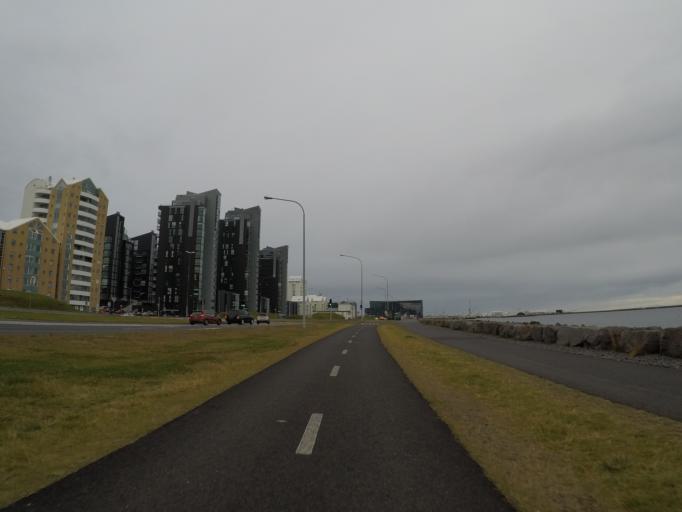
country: IS
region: Capital Region
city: Reykjavik
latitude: 64.1466
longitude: -21.9199
